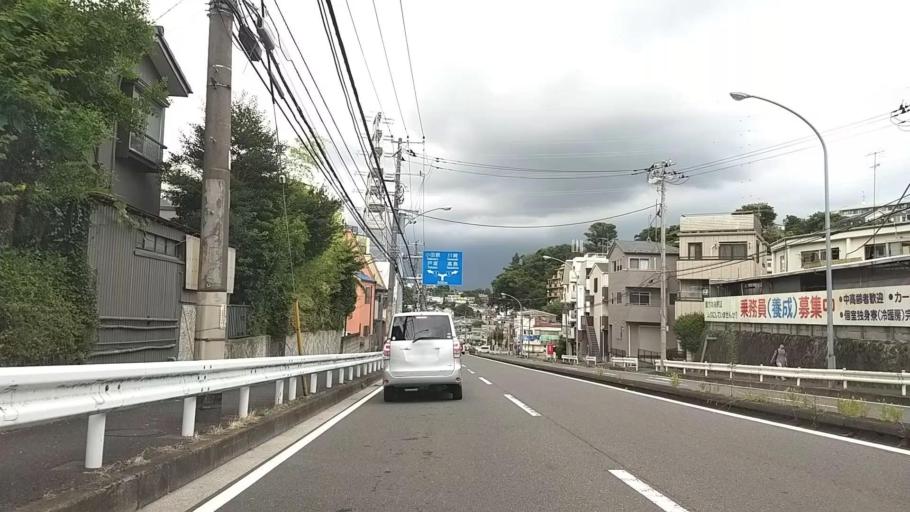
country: JP
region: Kanagawa
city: Yokohama
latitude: 35.4407
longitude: 139.5961
